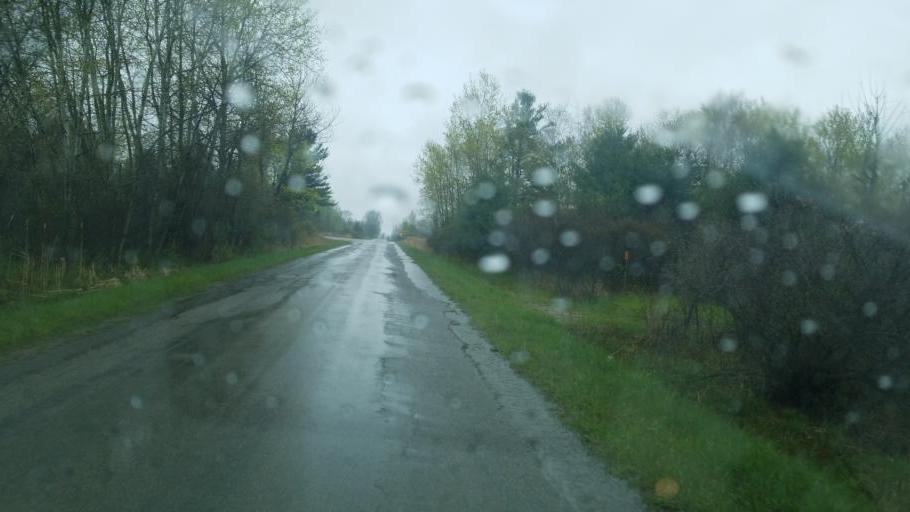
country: US
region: Michigan
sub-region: Montcalm County
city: Lakeview
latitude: 43.4519
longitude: -85.2933
